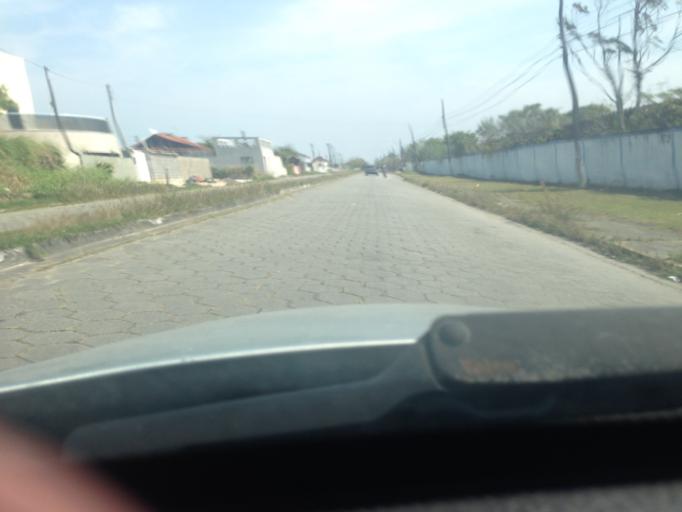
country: BR
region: Sao Paulo
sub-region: Itanhaem
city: Itanhaem
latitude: -24.2227
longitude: -46.8621
